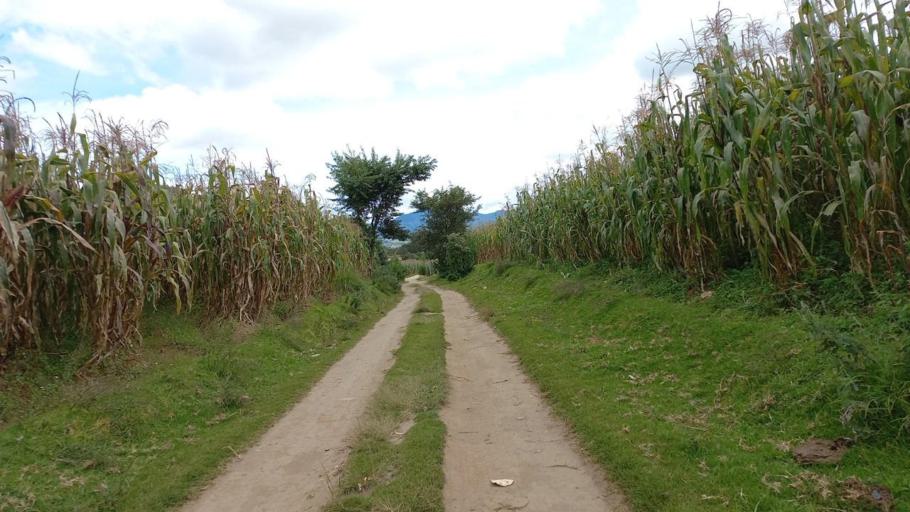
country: GT
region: Totonicapan
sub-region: Municipio de San Andres Xecul
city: San Andres Xecul
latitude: 14.8976
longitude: -91.4707
